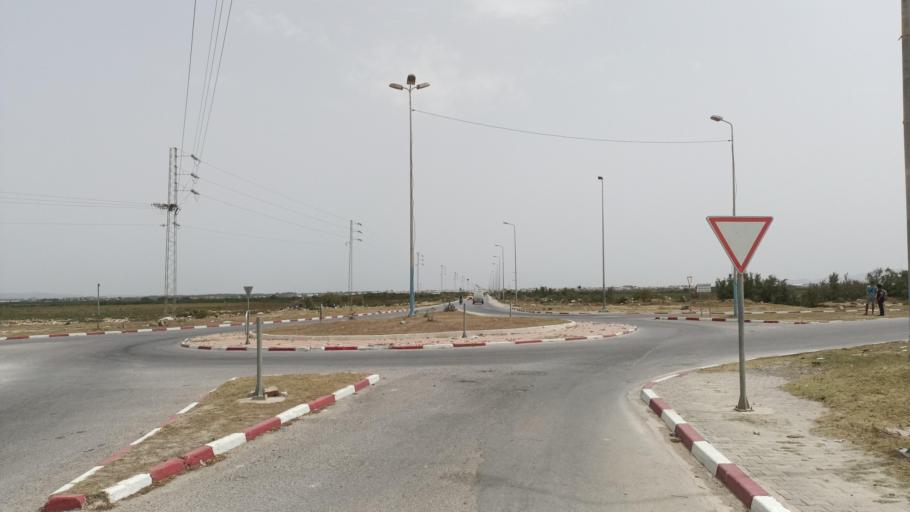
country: TN
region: Nabul
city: Manzil Bu Zalafah
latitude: 36.7264
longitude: 10.4698
